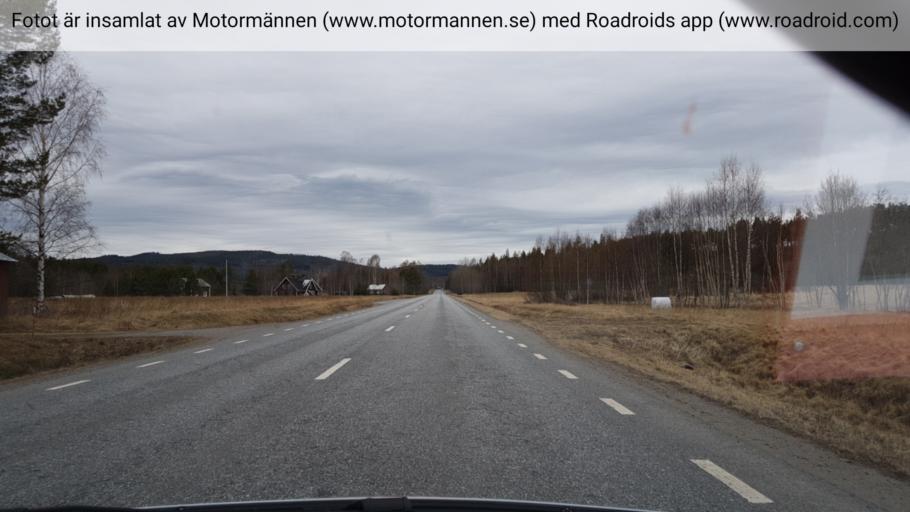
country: SE
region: Vaesternorrland
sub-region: Solleftea Kommun
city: Solleftea
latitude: 63.2617
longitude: 17.2157
